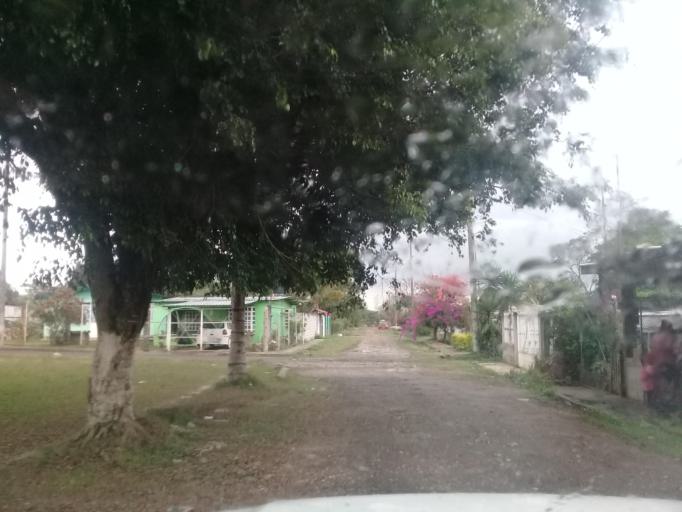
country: MX
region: Veracruz
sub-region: Amatlan de los Reyes
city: Trapiche Viejo
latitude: 18.8414
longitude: -96.9458
